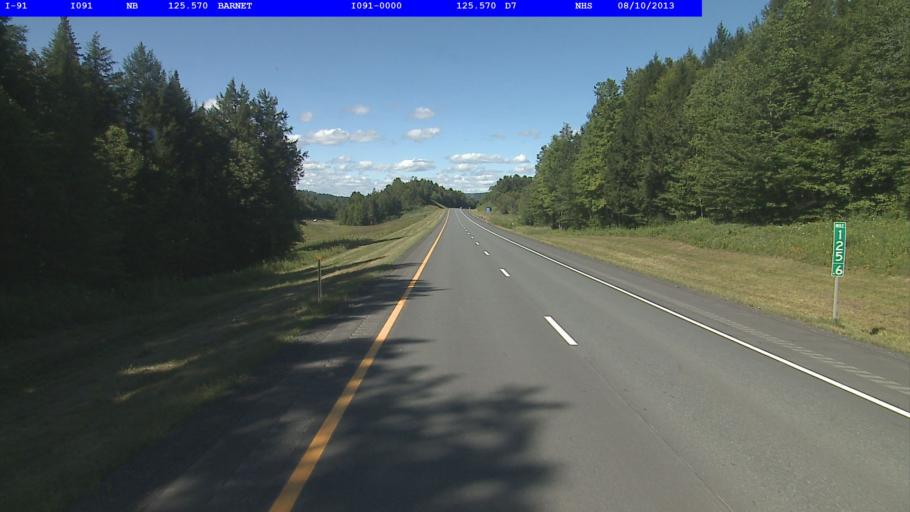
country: US
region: Vermont
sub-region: Caledonia County
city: Saint Johnsbury
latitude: 44.3601
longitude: -72.0318
